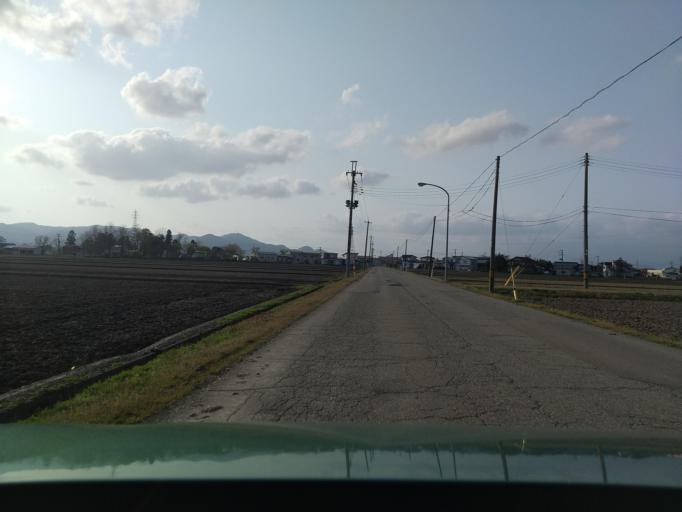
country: JP
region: Akita
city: Omagari
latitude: 39.4228
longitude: 140.4907
